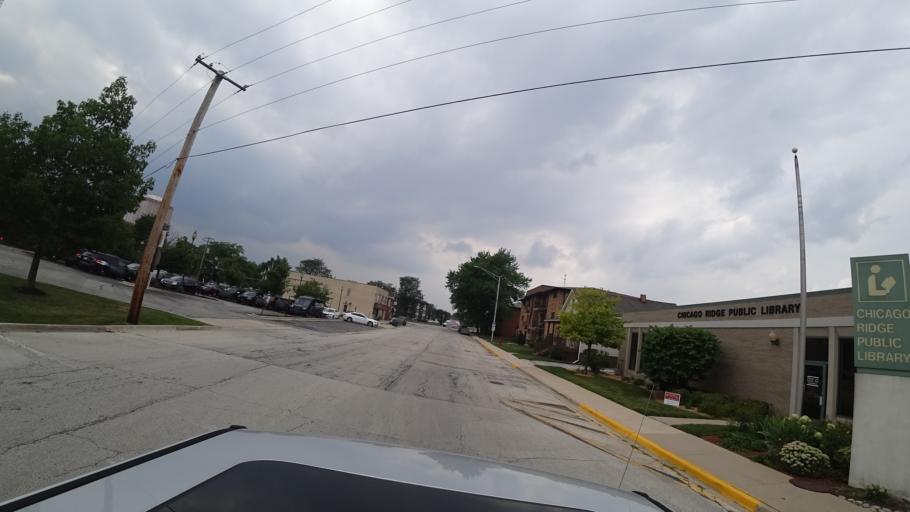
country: US
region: Illinois
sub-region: Cook County
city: Chicago Ridge
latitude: 41.7026
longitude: -87.7781
